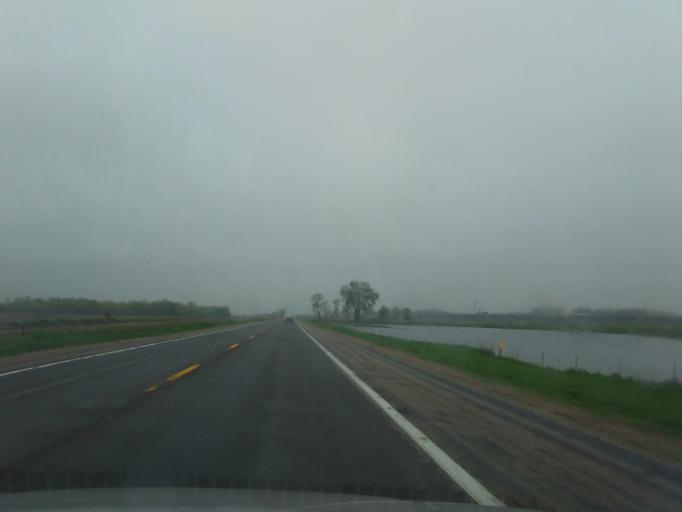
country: US
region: Nebraska
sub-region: Cuming County
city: Wisner
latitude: 41.9398
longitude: -96.8330
